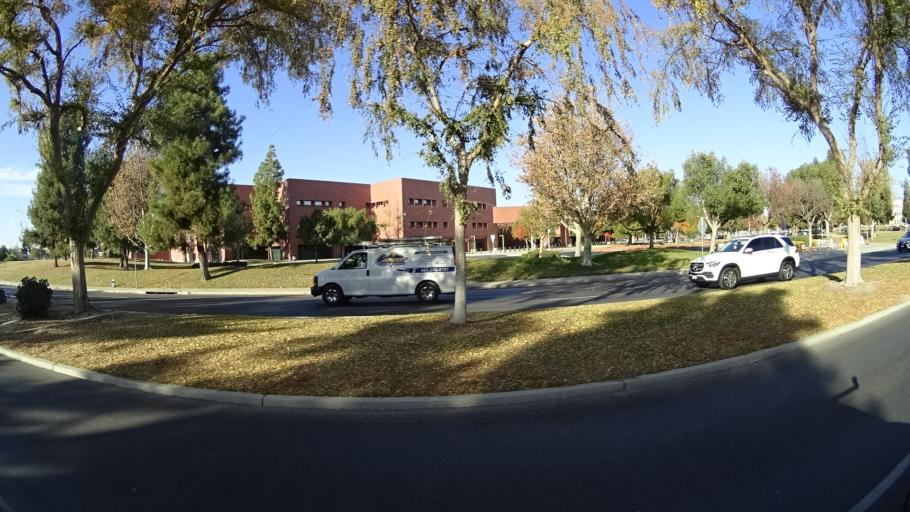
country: US
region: California
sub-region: Kern County
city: Greenacres
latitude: 35.3397
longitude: -119.1129
